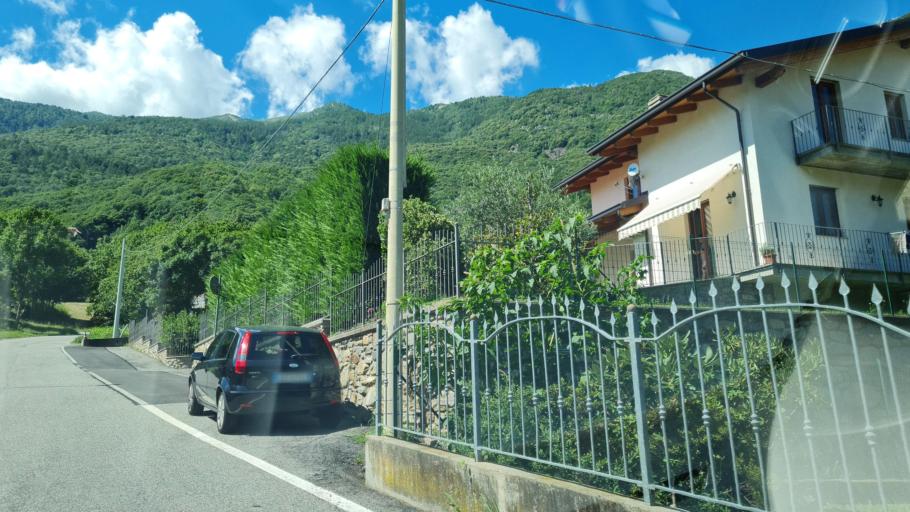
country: IT
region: Piedmont
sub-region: Provincia di Torino
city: Quincinetto
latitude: 45.5571
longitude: 7.8094
